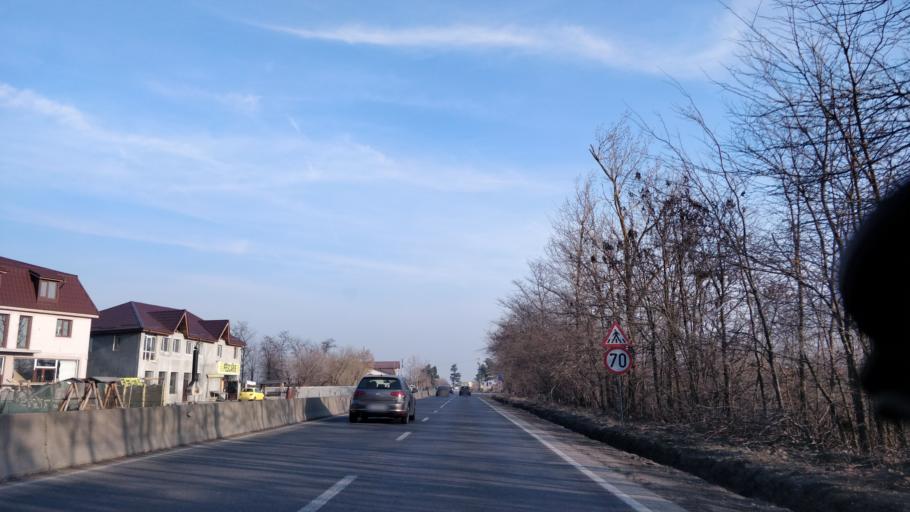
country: RO
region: Ilfov
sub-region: Comuna Buftea
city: Buciumeni
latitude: 44.5283
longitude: 25.9484
